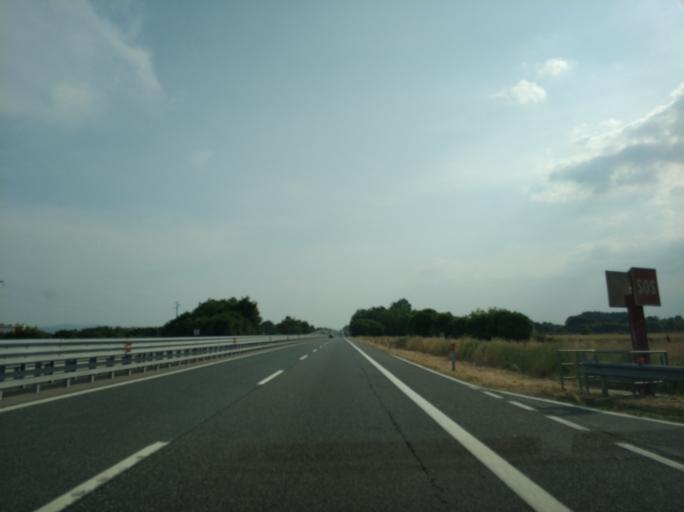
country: IT
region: Piedmont
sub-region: Provincia di Torino
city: Volpiano
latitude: 45.1850
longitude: 7.7798
